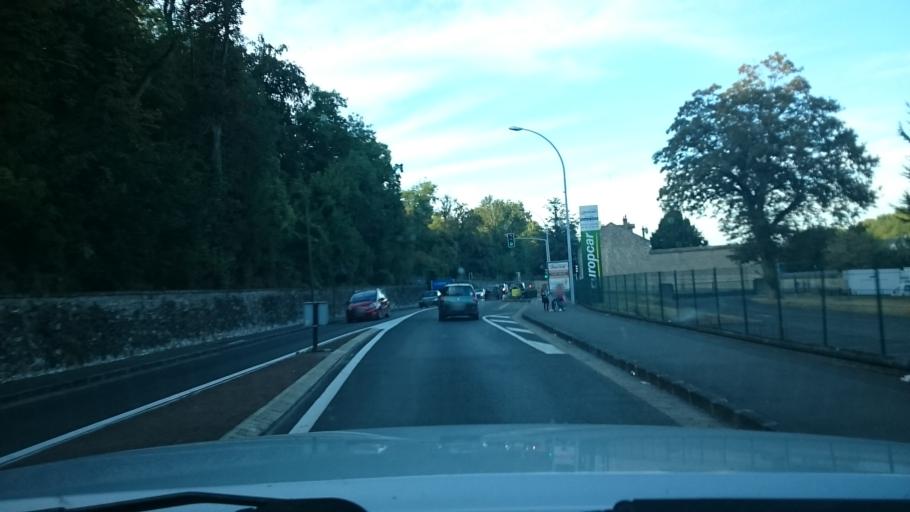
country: FR
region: Ile-de-France
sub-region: Departement de Seine-et-Marne
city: Samoreau
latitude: 48.4206
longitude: 2.7366
